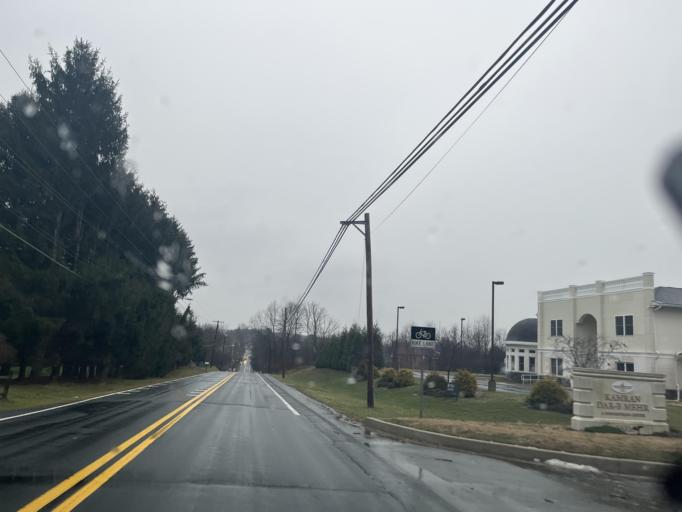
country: US
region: Maryland
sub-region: Montgomery County
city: Germantown
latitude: 39.1879
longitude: -77.3189
